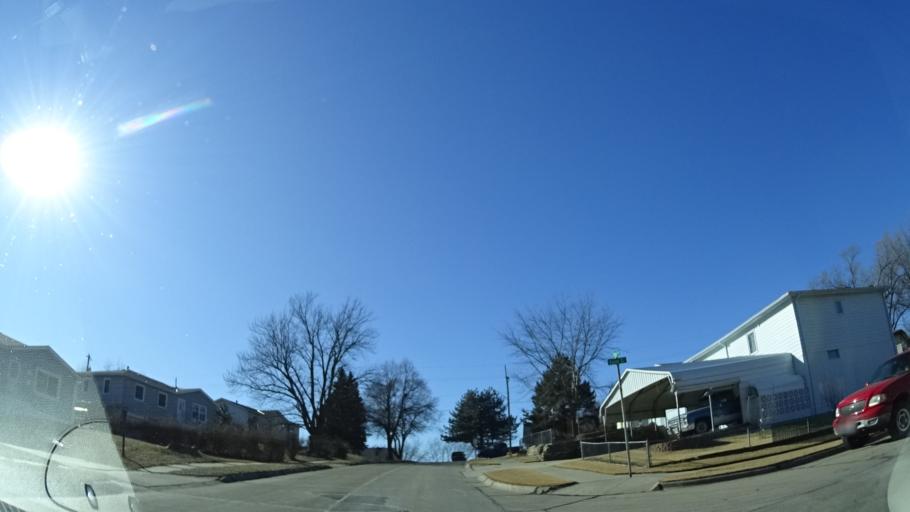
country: US
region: Nebraska
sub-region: Sarpy County
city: Bellevue
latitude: 41.1463
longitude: -95.9092
